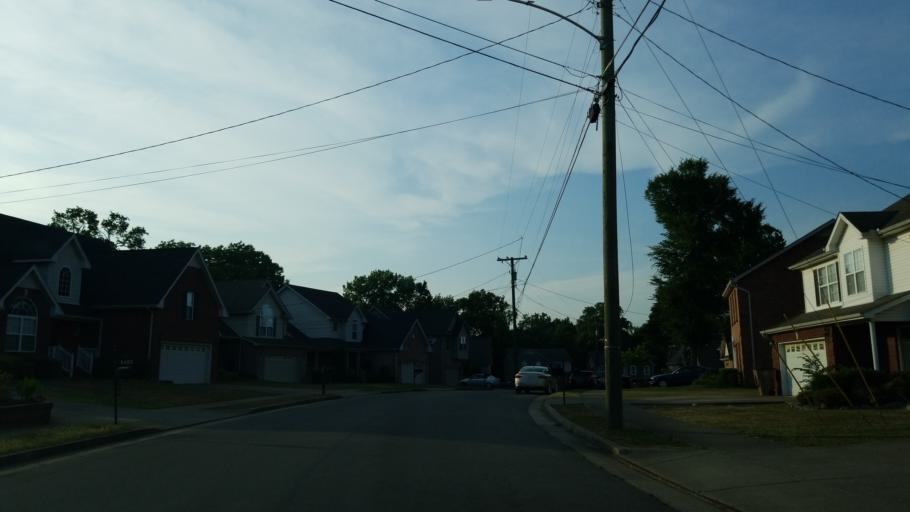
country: US
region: Tennessee
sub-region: Rutherford County
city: La Vergne
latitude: 36.0540
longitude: -86.5896
